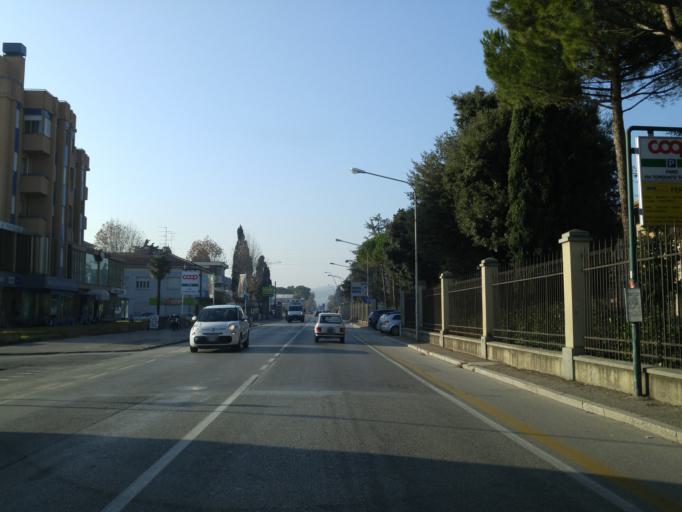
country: IT
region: The Marches
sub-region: Provincia di Pesaro e Urbino
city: Fano
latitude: 43.8381
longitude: 13.0084
